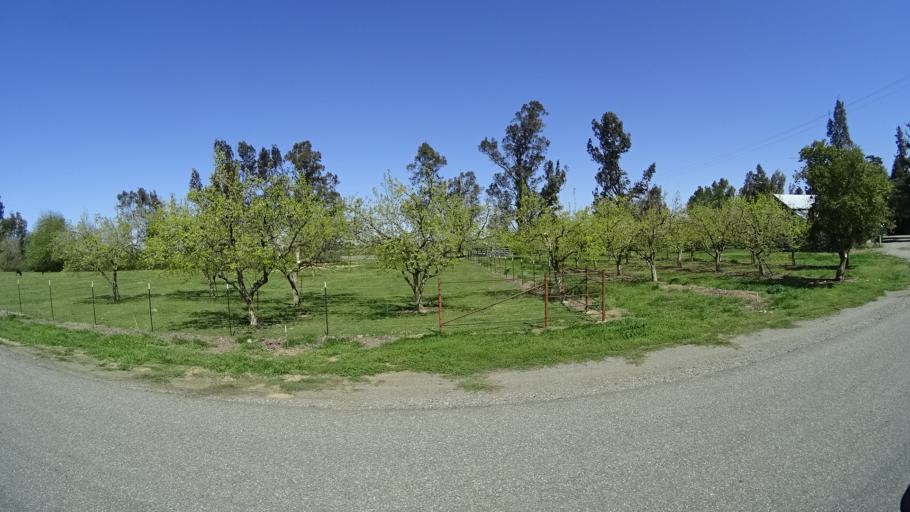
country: US
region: California
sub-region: Glenn County
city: Hamilton City
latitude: 39.7969
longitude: -122.0782
